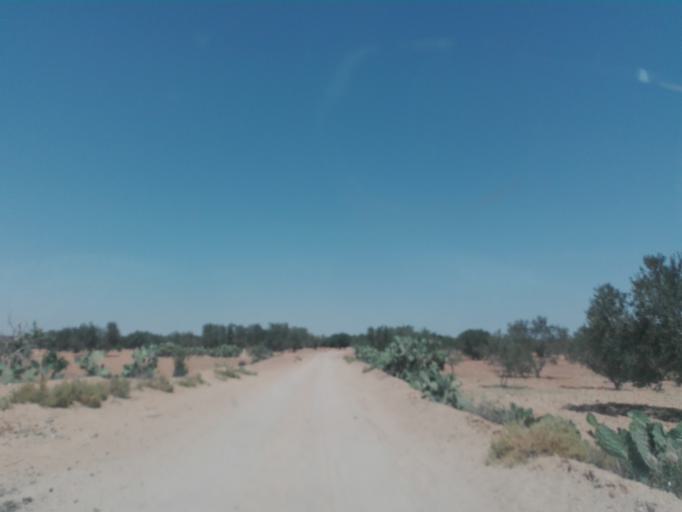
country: TN
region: Safaqis
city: Bi'r `Ali Bin Khalifah
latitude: 34.6469
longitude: 10.2598
